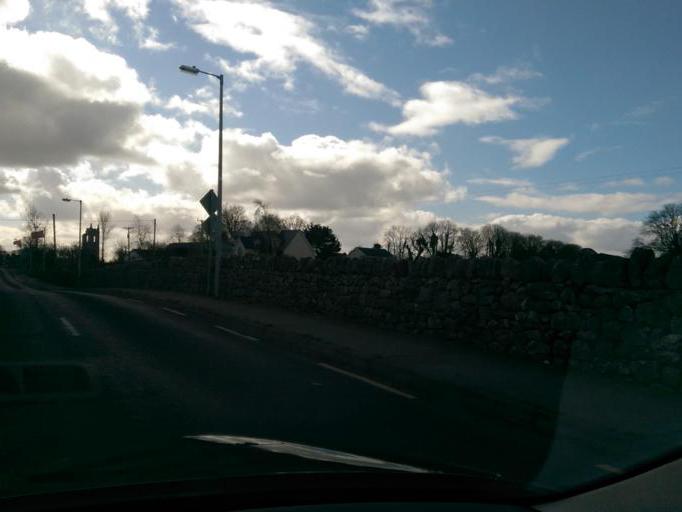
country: IE
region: Connaught
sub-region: County Galway
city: Athenry
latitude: 53.3762
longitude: -8.6991
